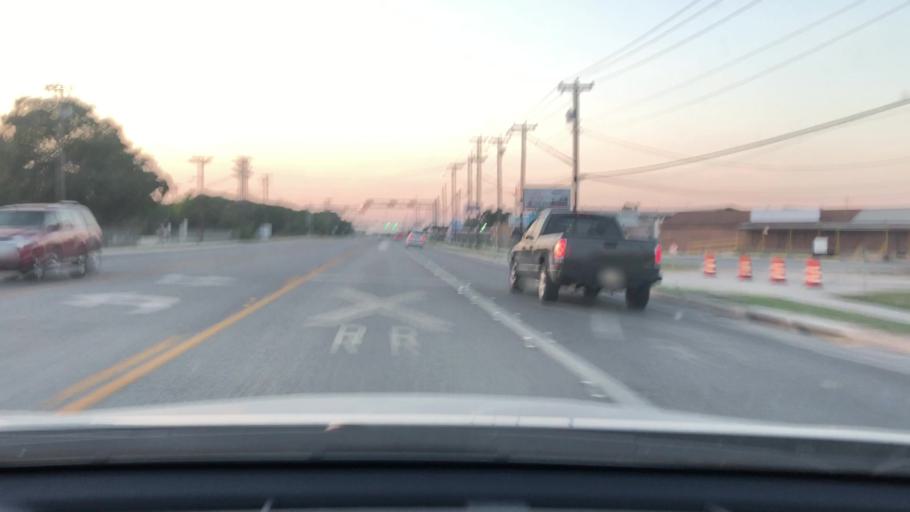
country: US
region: Texas
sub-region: Bexar County
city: Kirby
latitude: 29.4371
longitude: -98.4054
